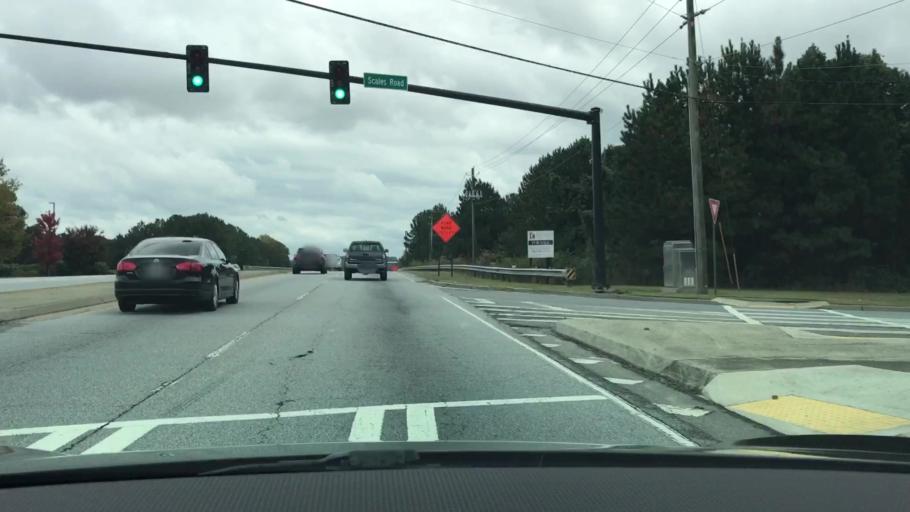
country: US
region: Georgia
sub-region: Gwinnett County
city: Suwanee
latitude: 34.0447
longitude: -84.0843
